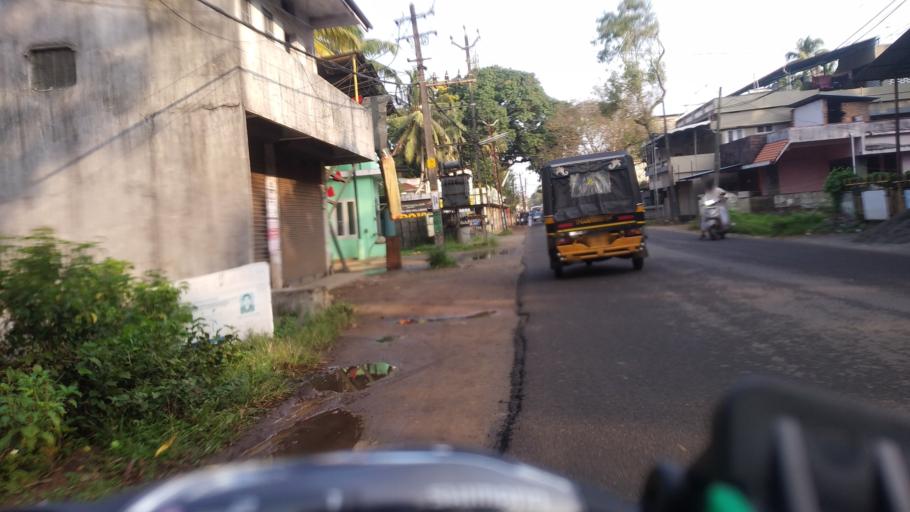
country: IN
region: Kerala
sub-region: Ernakulam
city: Elur
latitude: 10.0777
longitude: 76.2108
